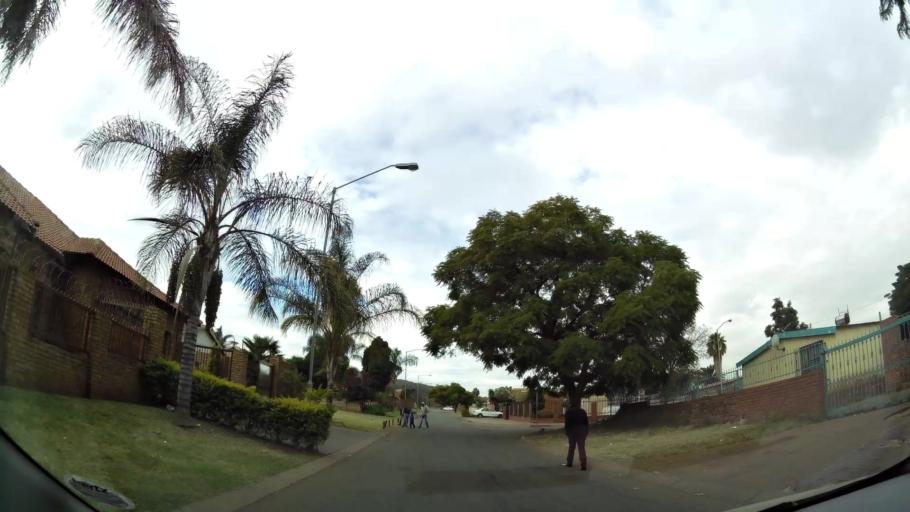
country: ZA
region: Gauteng
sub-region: City of Tshwane Metropolitan Municipality
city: Pretoria
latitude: -25.6997
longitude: 28.3015
